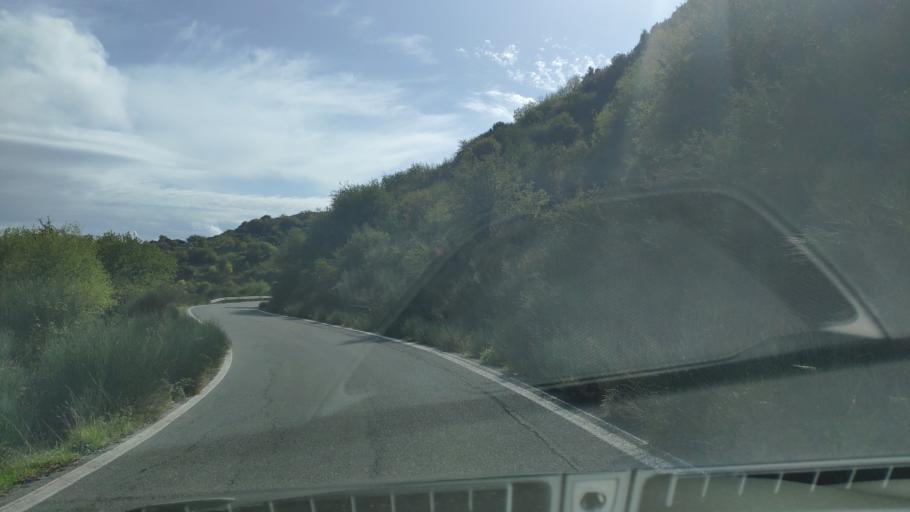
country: GR
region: Peloponnese
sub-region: Nomos Arkadias
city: Dimitsana
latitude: 37.5817
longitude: 22.0171
